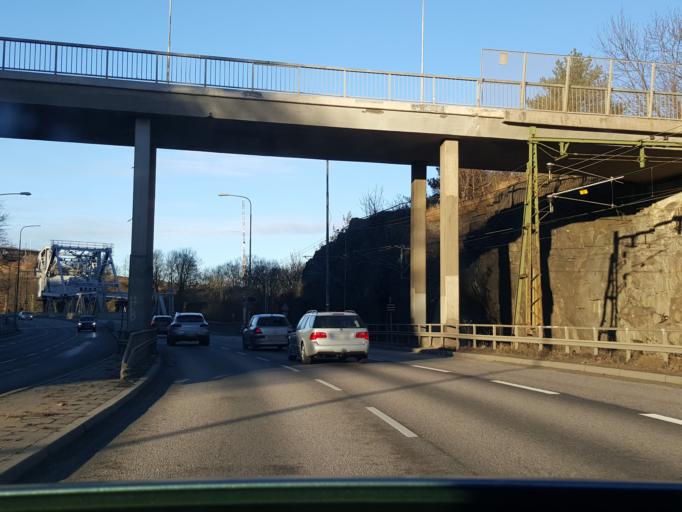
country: SE
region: Stockholm
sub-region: Stockholms Kommun
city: OEstermalm
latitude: 59.3127
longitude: 18.1070
